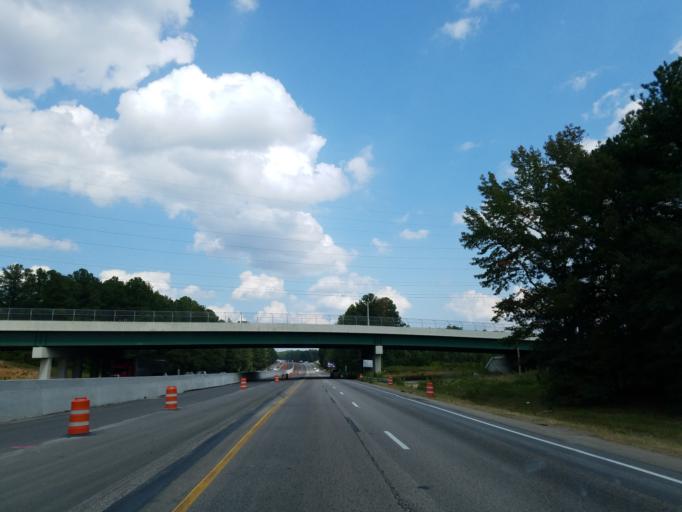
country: US
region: Georgia
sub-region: Gwinnett County
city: Buford
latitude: 34.0628
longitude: -83.9481
